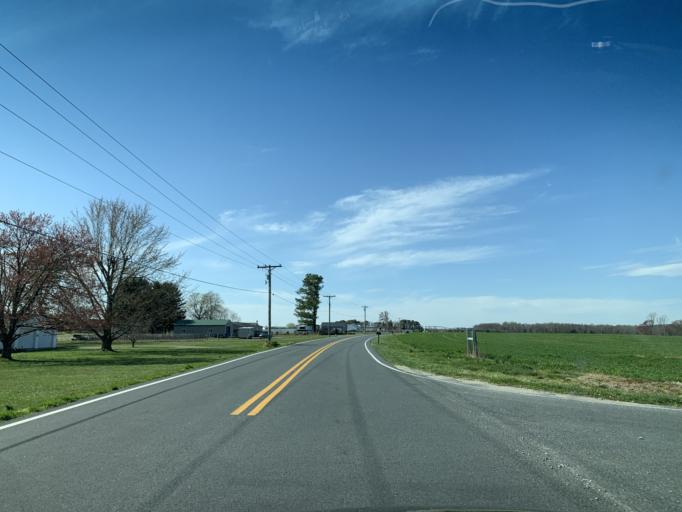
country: US
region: Delaware
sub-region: Kent County
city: Riverview
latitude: 39.0139
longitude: -75.5332
